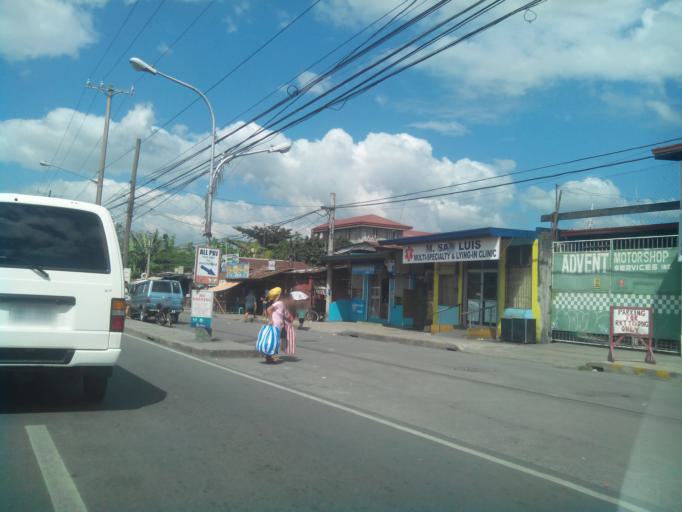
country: PH
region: Calabarzon
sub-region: Province of Rizal
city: Taytay
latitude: 14.5441
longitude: 121.1442
